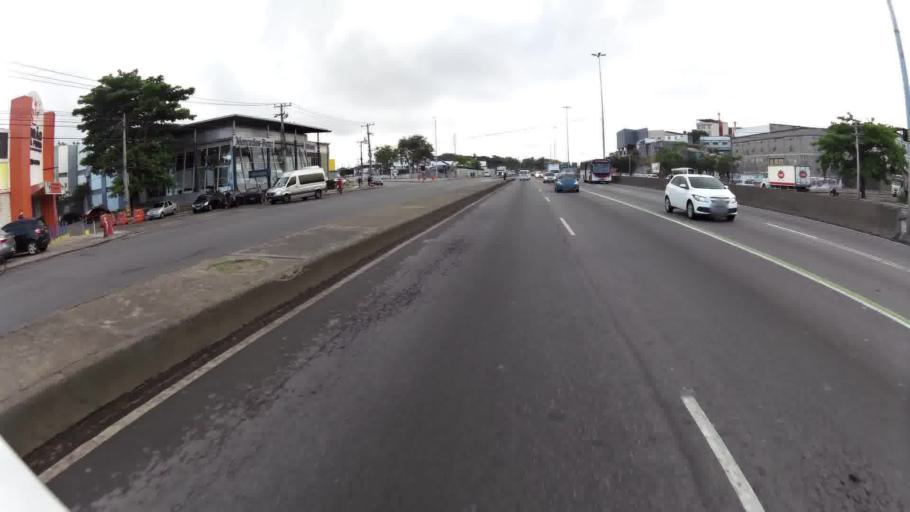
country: BR
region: Rio de Janeiro
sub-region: Rio De Janeiro
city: Rio de Janeiro
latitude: -22.8441
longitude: -43.2498
